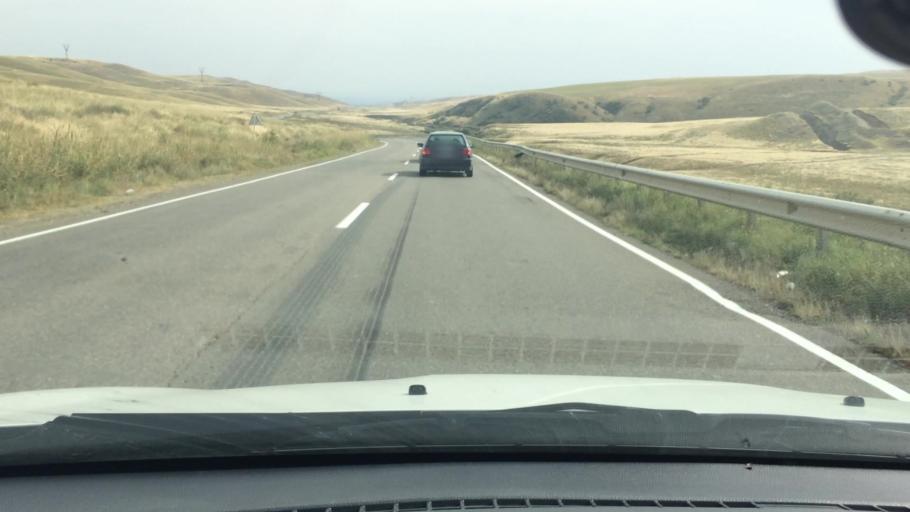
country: GE
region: Kvemo Kartli
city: Rust'avi
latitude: 41.5228
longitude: 44.9373
